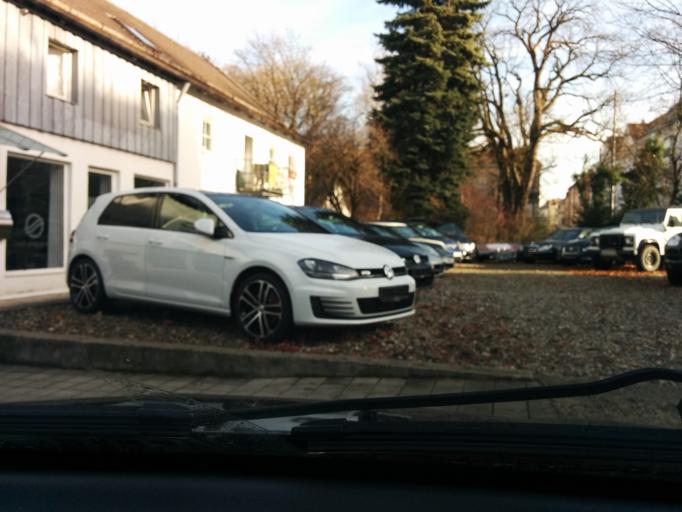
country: DE
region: Bavaria
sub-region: Upper Bavaria
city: Pasing
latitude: 48.1476
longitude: 11.4560
